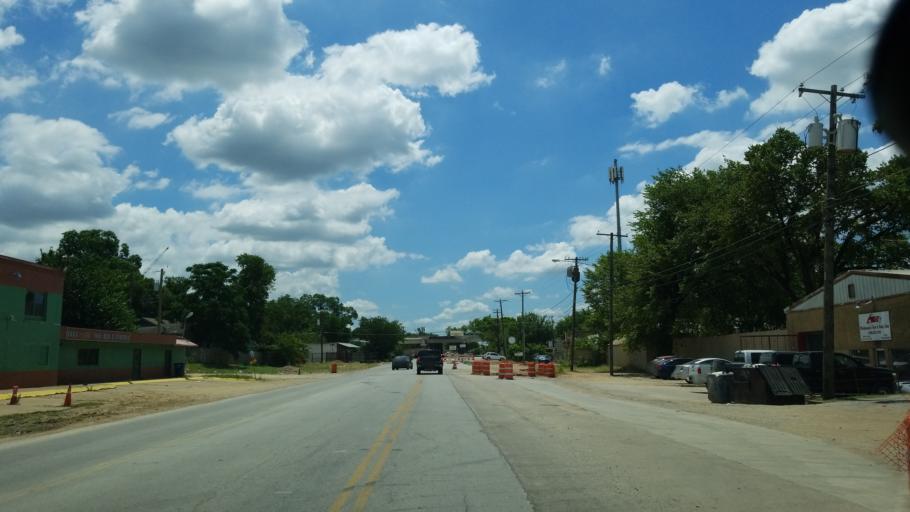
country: US
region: Texas
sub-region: Dallas County
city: Dallas
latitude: 32.7468
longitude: -96.7632
